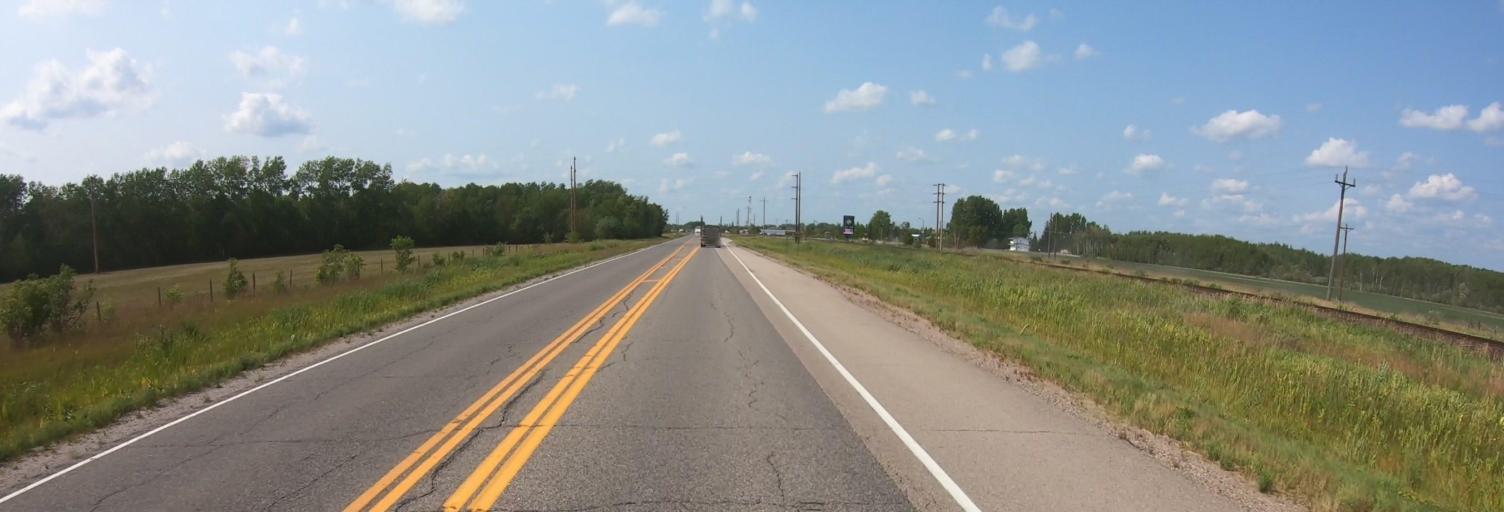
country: US
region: Minnesota
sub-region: Roseau County
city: Warroad
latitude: 48.8913
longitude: -95.3069
